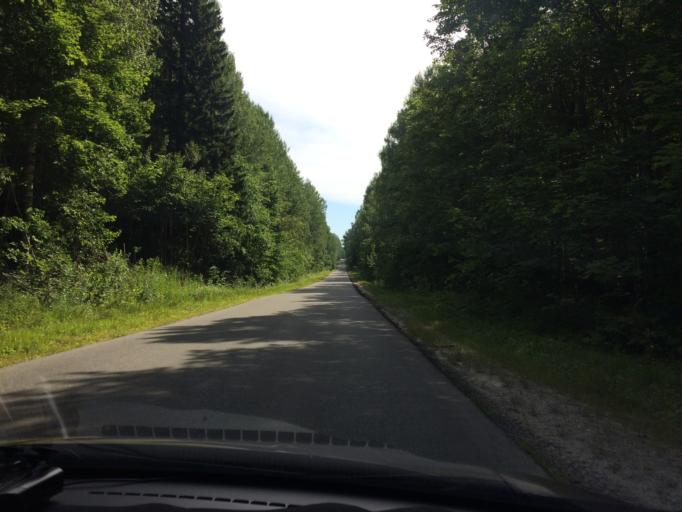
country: RU
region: Mariy-El
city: Surok
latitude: 56.5713
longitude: 48.1414
